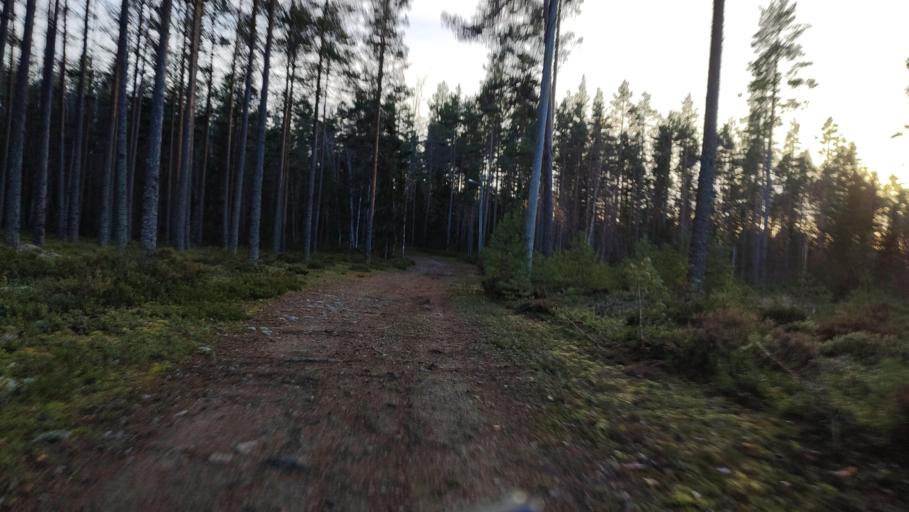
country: FI
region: Southern Ostrobothnia
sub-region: Suupohja
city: Karijoki
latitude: 62.2770
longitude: 21.6288
